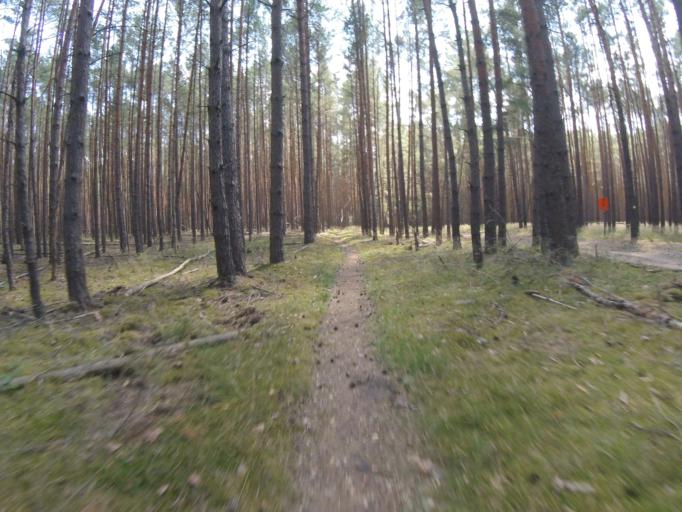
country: DE
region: Brandenburg
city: Bestensee
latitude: 52.2694
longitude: 13.6959
